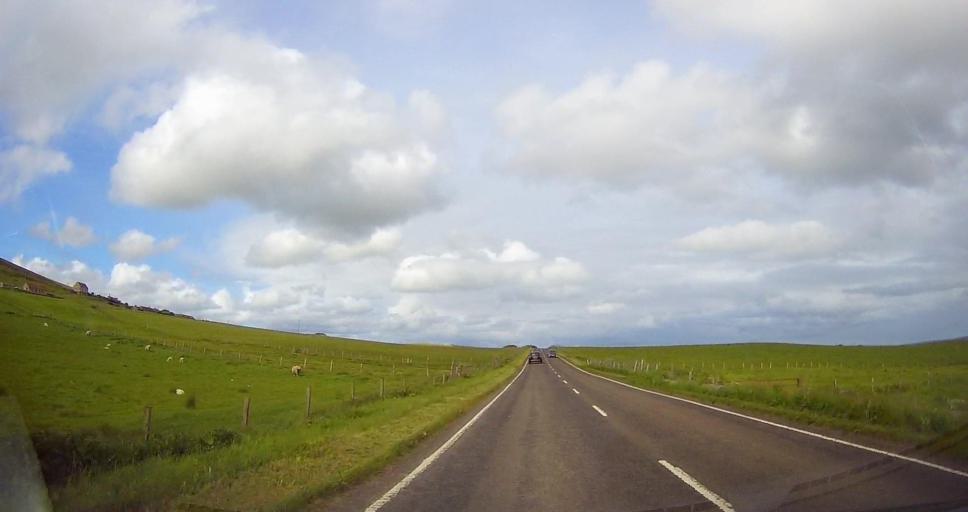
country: GB
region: Scotland
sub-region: Orkney Islands
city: Orkney
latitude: 59.0167
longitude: -3.1051
